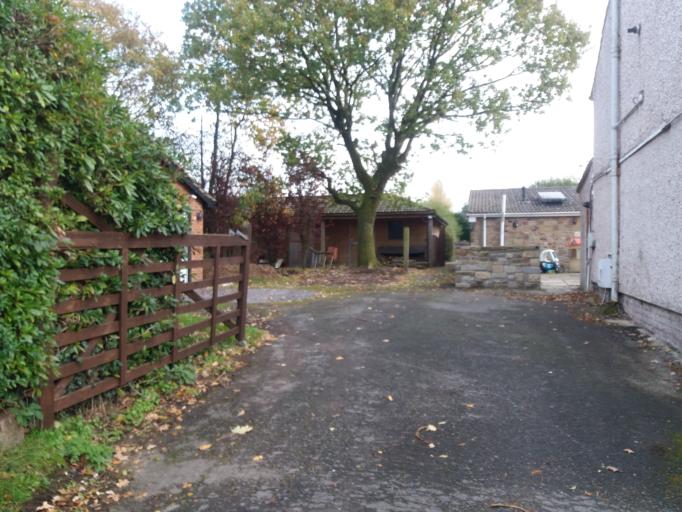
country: GB
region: England
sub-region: Lancashire
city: Coppull
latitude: 53.6117
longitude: -2.6581
